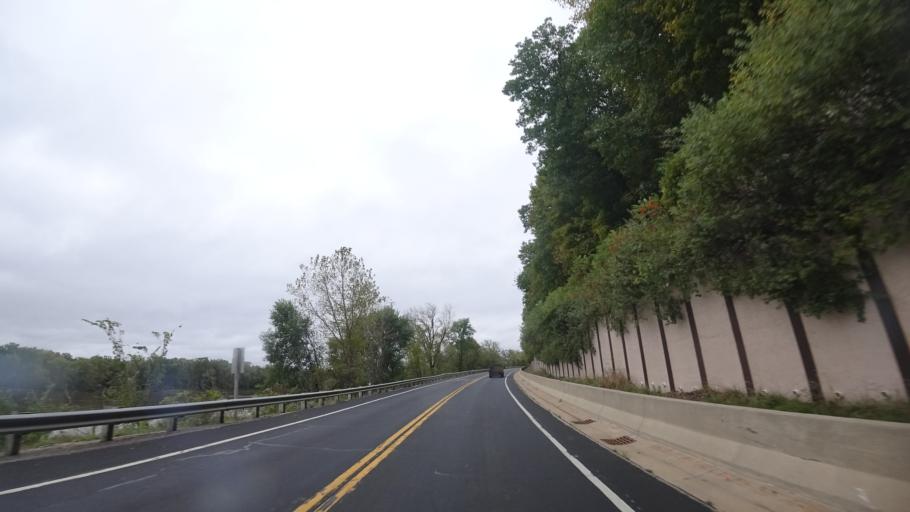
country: US
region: Wisconsin
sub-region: Grant County
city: Boscobel
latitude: 43.1490
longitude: -90.7225
